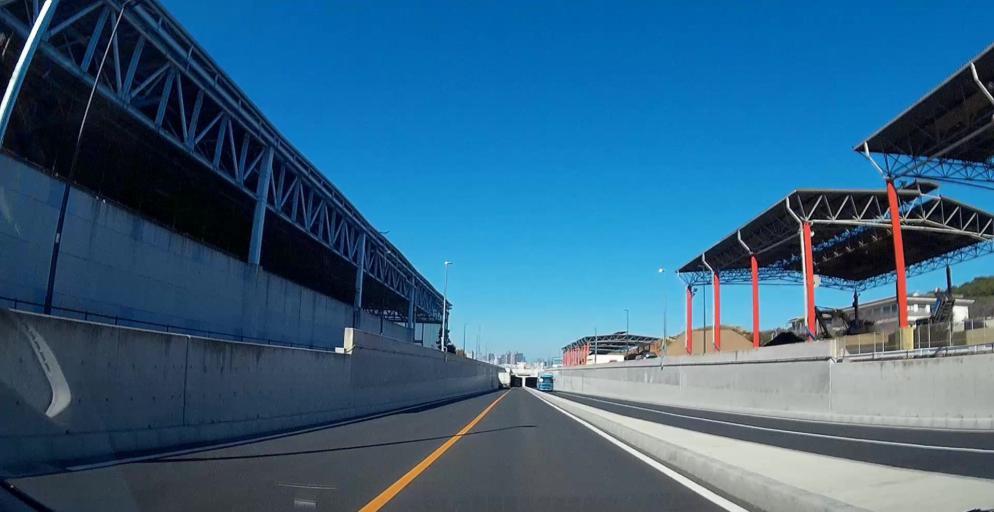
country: JP
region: Tokyo
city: Urayasu
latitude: 35.6026
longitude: 139.8033
